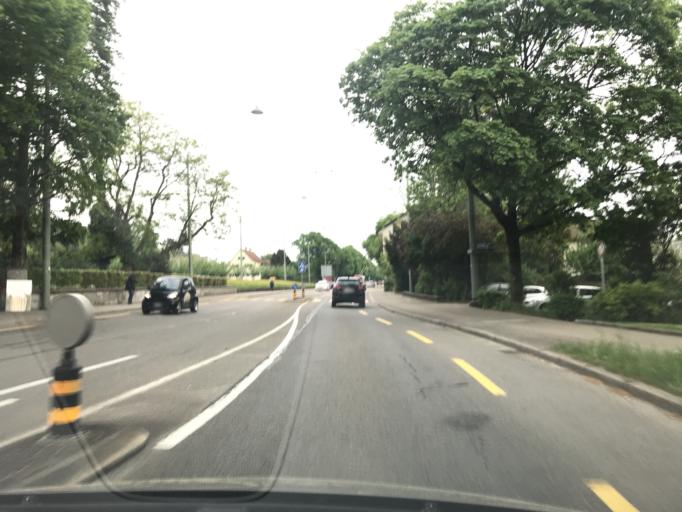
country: CH
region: Zurich
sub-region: Bezirk Winterthur
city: Wuelflingen (Kreis 6) / Lindenplatz
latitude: 47.5110
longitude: 8.6989
